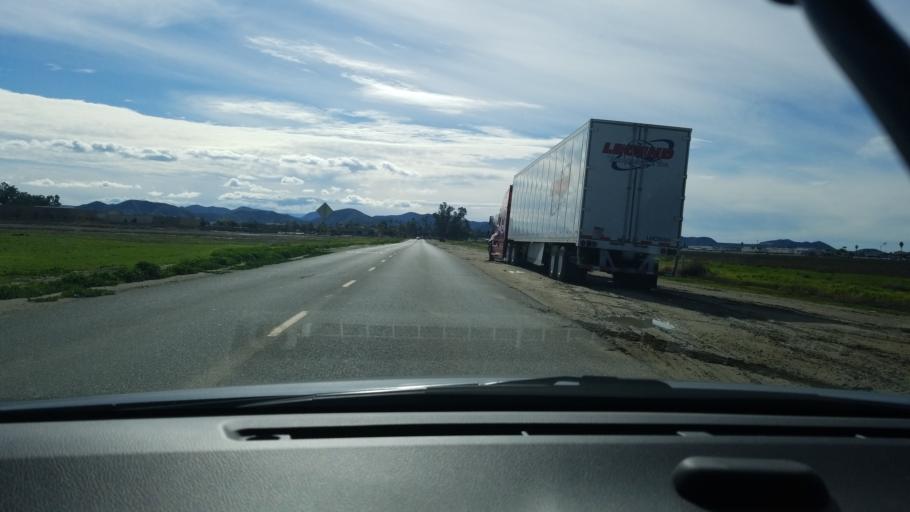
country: US
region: California
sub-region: Riverside County
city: Hemet
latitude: 33.7504
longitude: -117.0241
